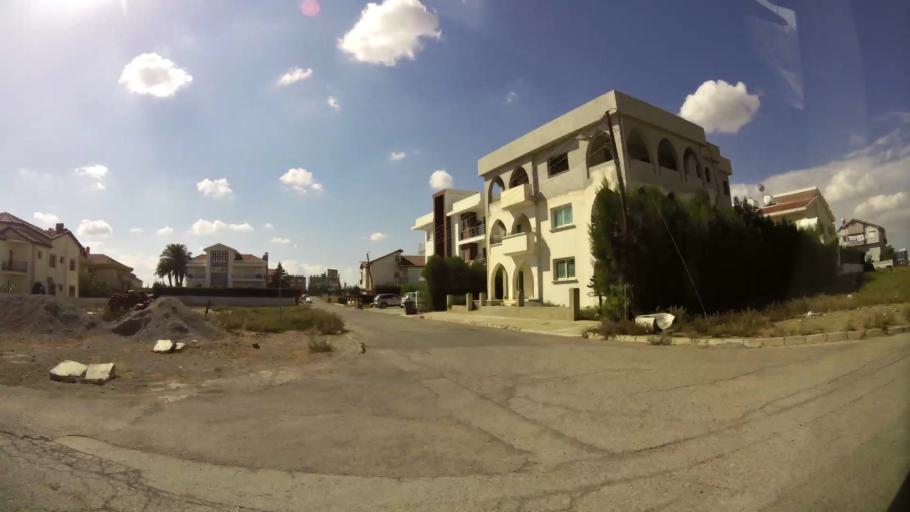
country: CY
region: Lefkosia
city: Nicosia
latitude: 35.2098
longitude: 33.3257
